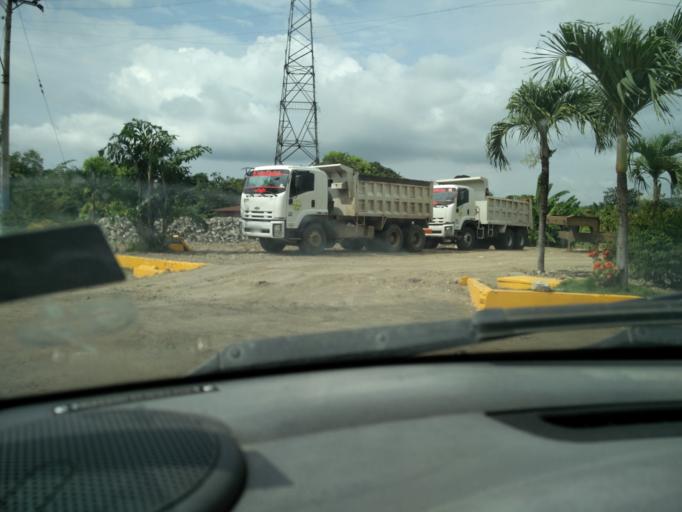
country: EC
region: Manabi
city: Portoviejo
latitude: -1.0102
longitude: -80.4655
